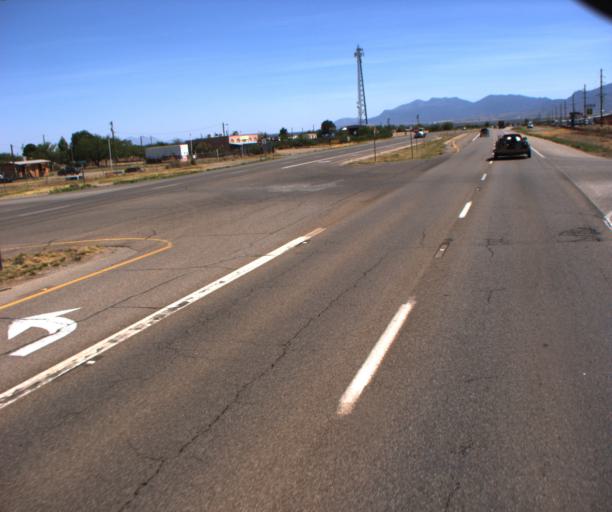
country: US
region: Arizona
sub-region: Cochise County
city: Huachuca City
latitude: 31.6872
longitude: -110.3505
